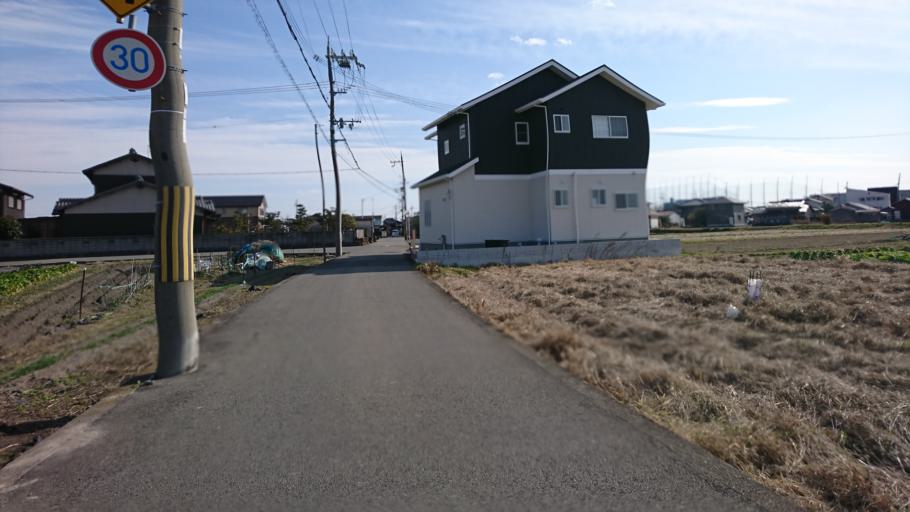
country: JP
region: Hyogo
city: Kakogawacho-honmachi
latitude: 34.7836
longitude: 134.8350
